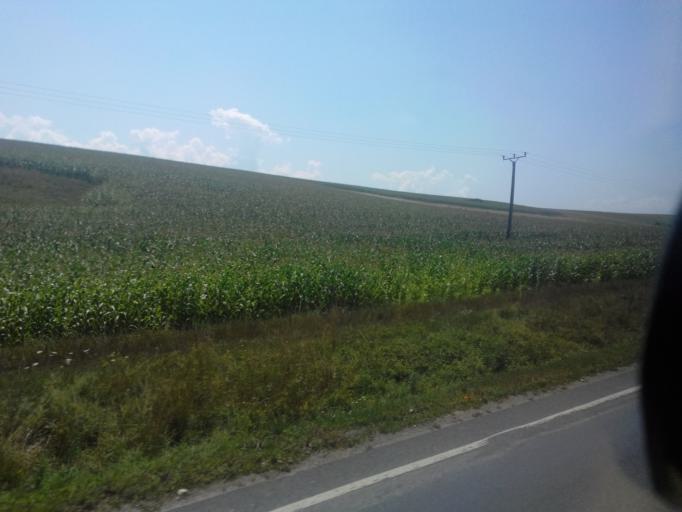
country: RO
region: Hunedoara
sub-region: Municipiul Orastie
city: Orastie
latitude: 45.8677
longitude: 23.2256
